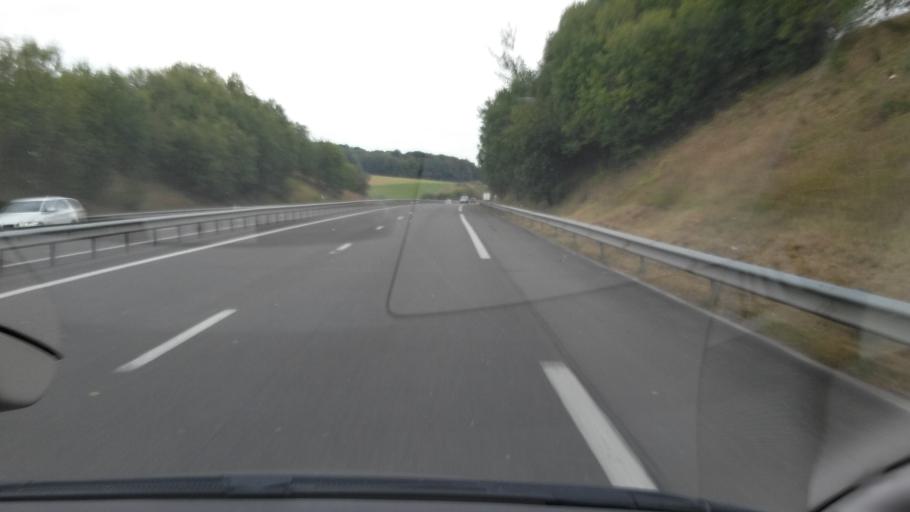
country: FR
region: Champagne-Ardenne
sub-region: Departement des Ardennes
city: La Francheville
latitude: 49.6546
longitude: 4.6346
